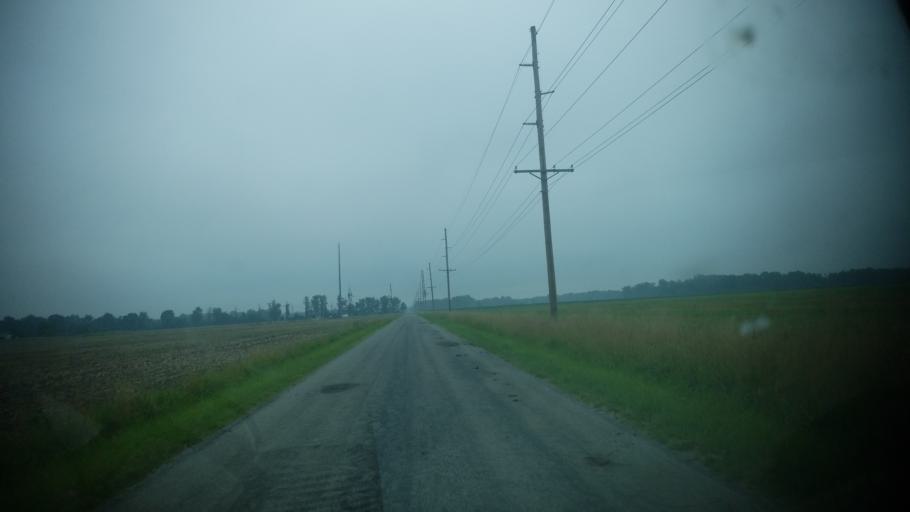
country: US
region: Illinois
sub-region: Clay County
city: Flora
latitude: 38.5417
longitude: -88.4021
